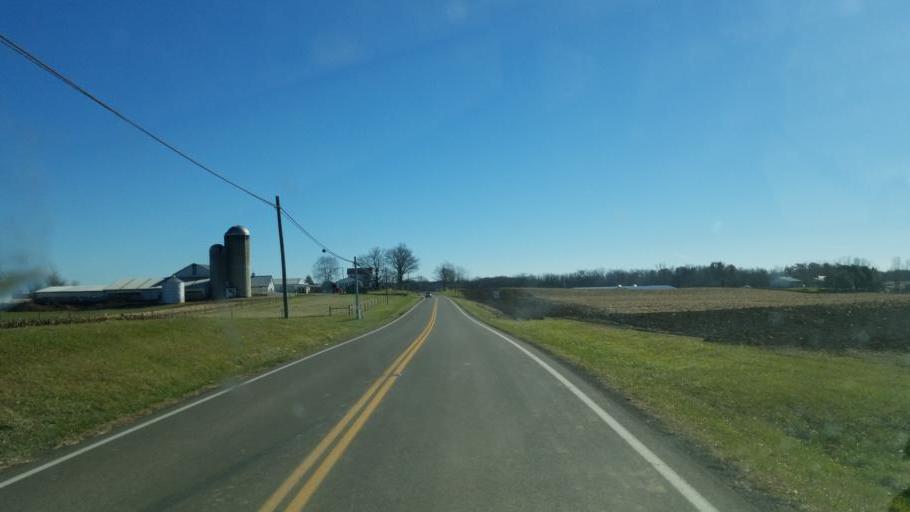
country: US
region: Ohio
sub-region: Huron County
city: Plymouth
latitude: 40.9631
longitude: -82.5941
